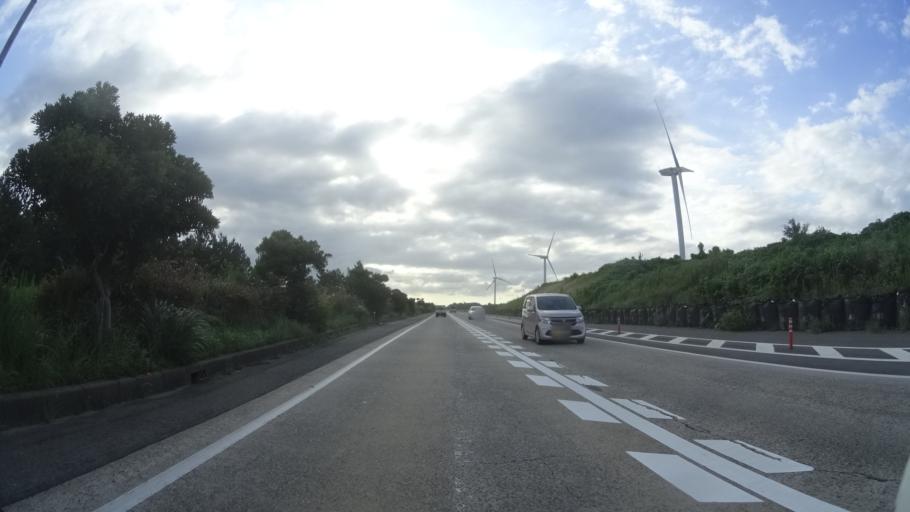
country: JP
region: Tottori
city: Kurayoshi
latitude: 35.4985
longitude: 133.8024
